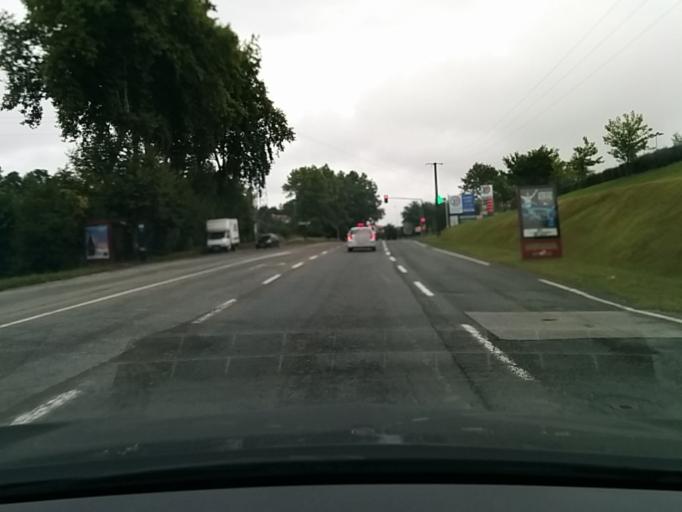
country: FR
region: Aquitaine
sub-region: Departement des Pyrenees-Atlantiques
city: Ciboure
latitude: 43.3747
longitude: -1.6788
